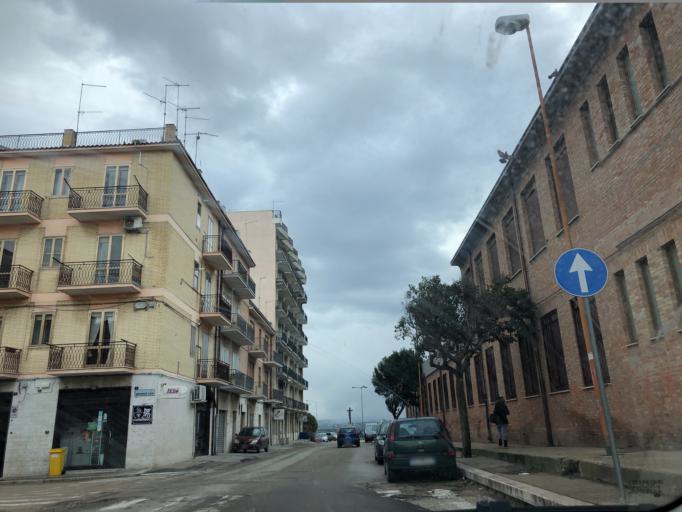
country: IT
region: Apulia
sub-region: Provincia di Foggia
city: Lucera
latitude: 41.5050
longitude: 15.3384
